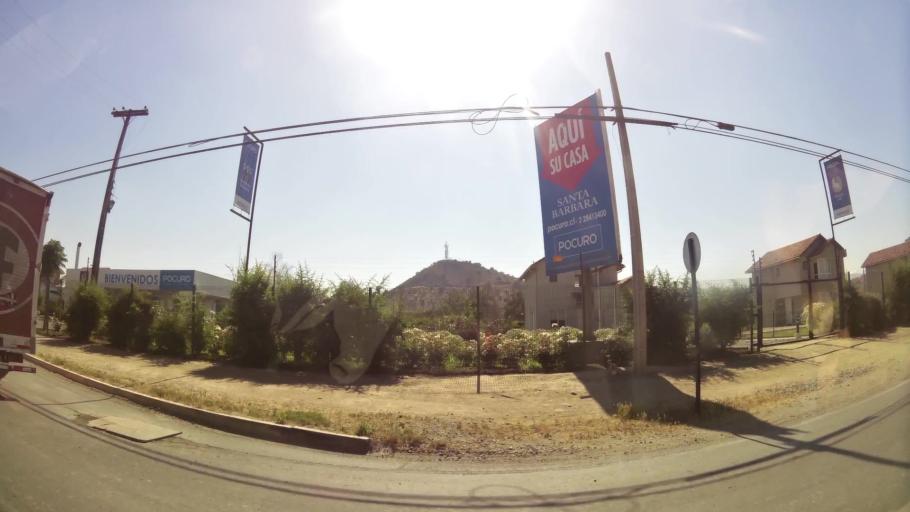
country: CL
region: Santiago Metropolitan
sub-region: Provincia de Maipo
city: San Bernardo
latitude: -33.6152
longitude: -70.6826
